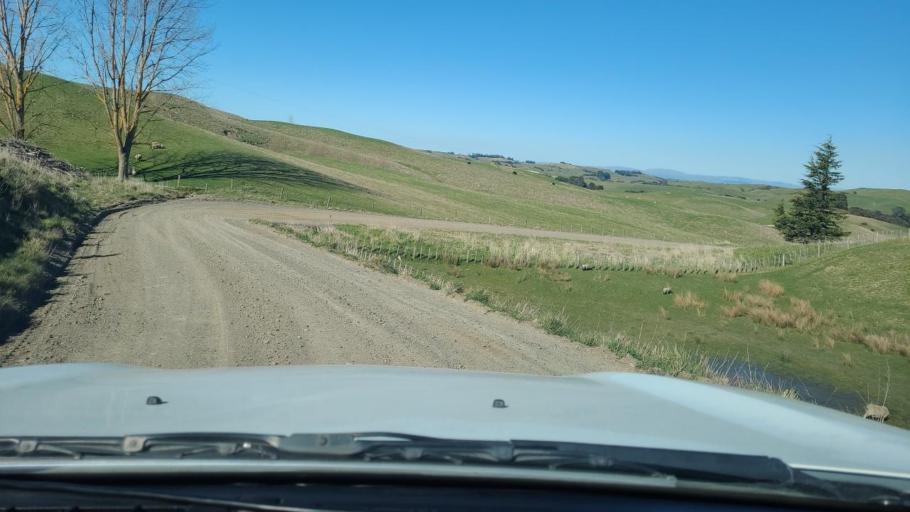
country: NZ
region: Hawke's Bay
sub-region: Napier City
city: Taradale
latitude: -39.5112
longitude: 176.5099
